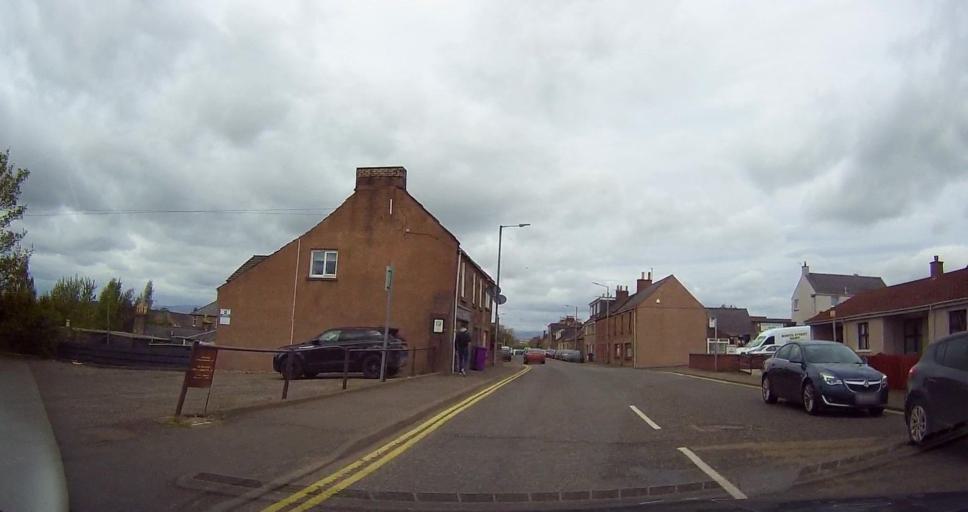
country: GB
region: Scotland
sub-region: Angus
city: Forfar
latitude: 56.6461
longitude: -2.8811
